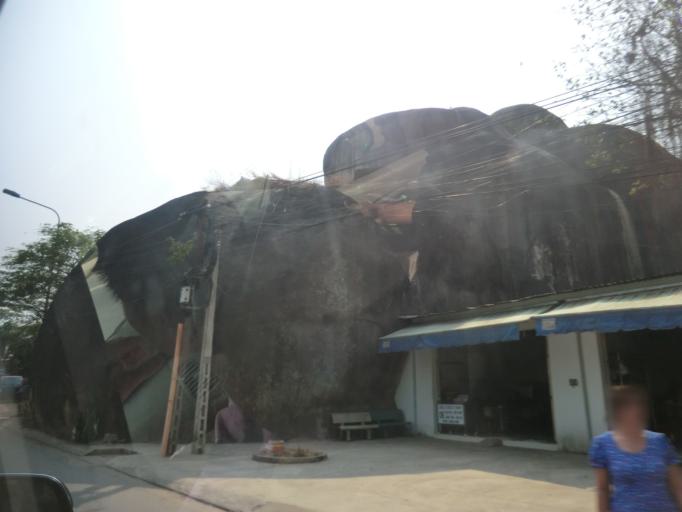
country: VN
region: Dong Nai
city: Tan Phu
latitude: 11.1965
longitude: 107.3521
